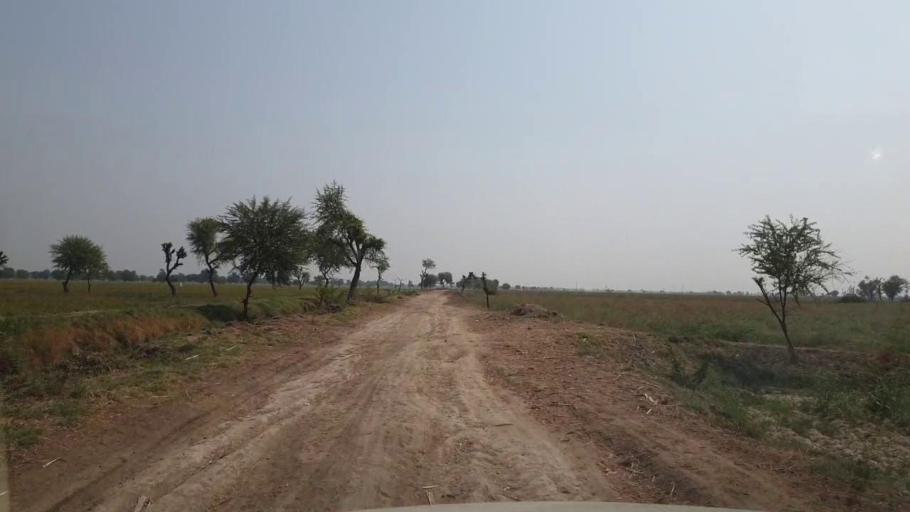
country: PK
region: Sindh
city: Chor
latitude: 25.4587
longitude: 69.6755
